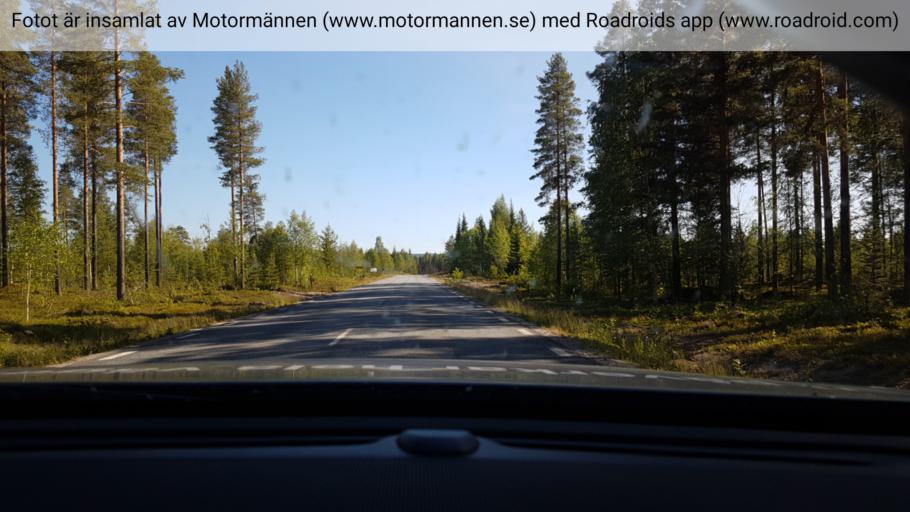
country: SE
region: Vaesterbotten
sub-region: Lycksele Kommun
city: Lycksele
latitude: 64.4932
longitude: 18.8974
